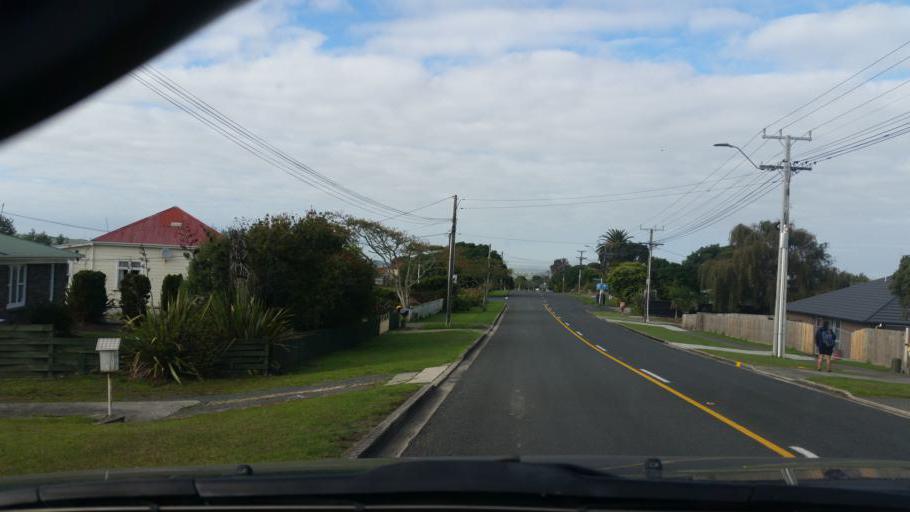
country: NZ
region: Northland
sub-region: Kaipara District
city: Dargaville
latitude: -35.9300
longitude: 173.8707
